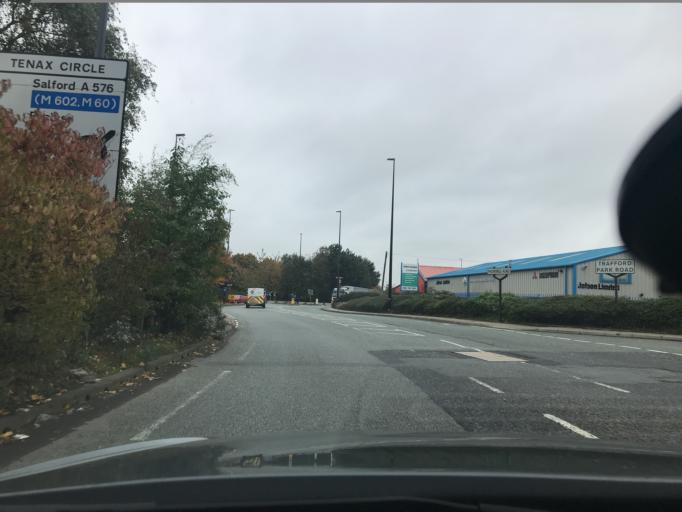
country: GB
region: England
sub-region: Trafford
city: Trafford Park
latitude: 53.4748
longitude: -2.3205
